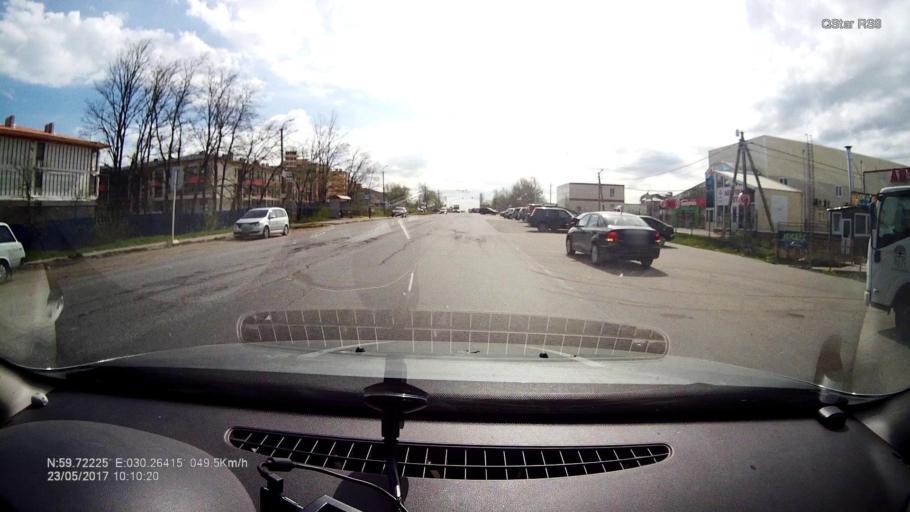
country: RU
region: St.-Petersburg
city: Aleksandrovskaya
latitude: 59.7222
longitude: 30.2642
